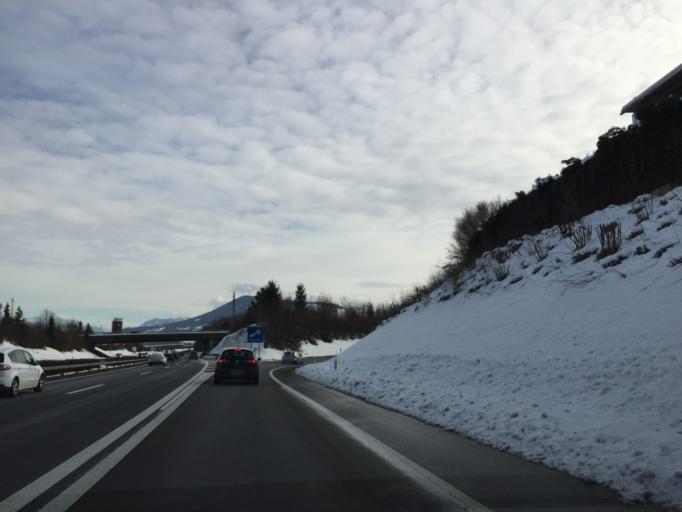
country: CH
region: Zurich
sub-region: Bezirk Horgen
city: Richterswil / Burghalde
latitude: 47.2035
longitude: 8.6829
